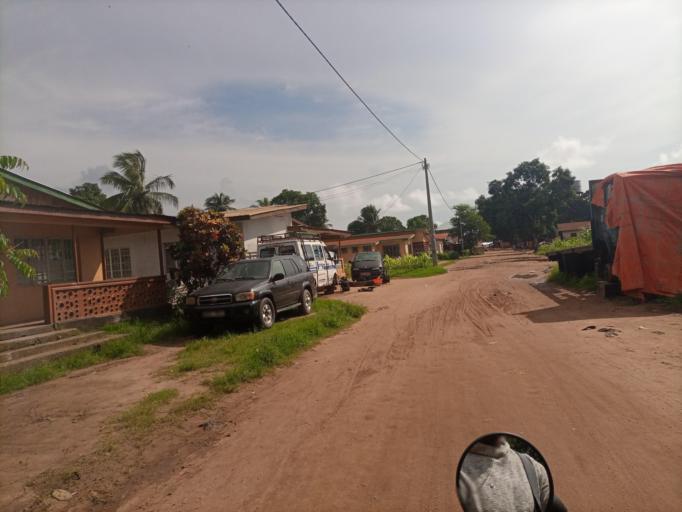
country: SL
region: Northern Province
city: Masoyila
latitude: 8.6051
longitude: -13.1771
